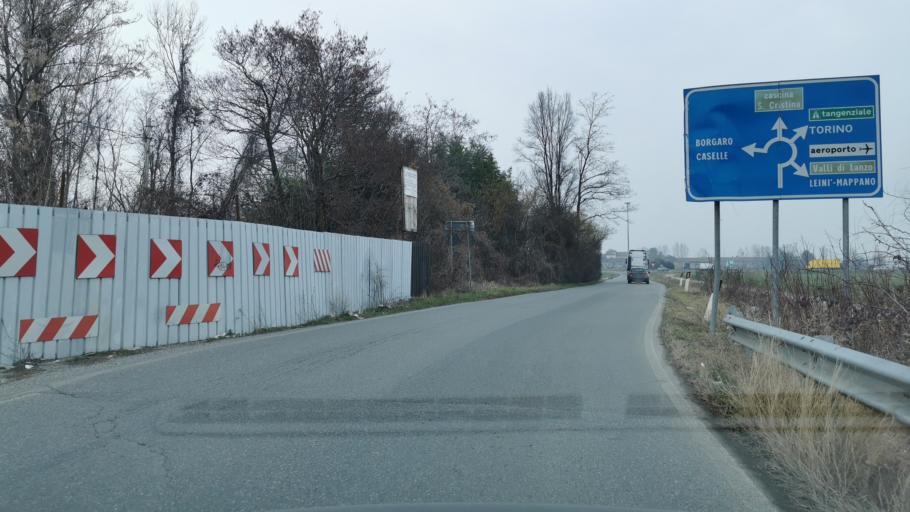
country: IT
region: Piedmont
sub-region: Provincia di Torino
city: Borgaro Torinese
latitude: 45.1381
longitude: 7.6853
